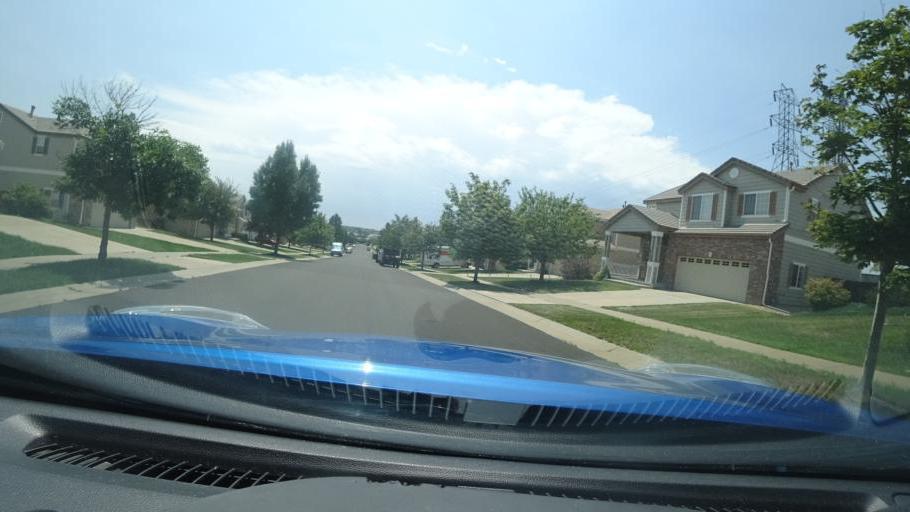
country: US
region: Colorado
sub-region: Adams County
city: Aurora
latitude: 39.6737
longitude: -104.7713
